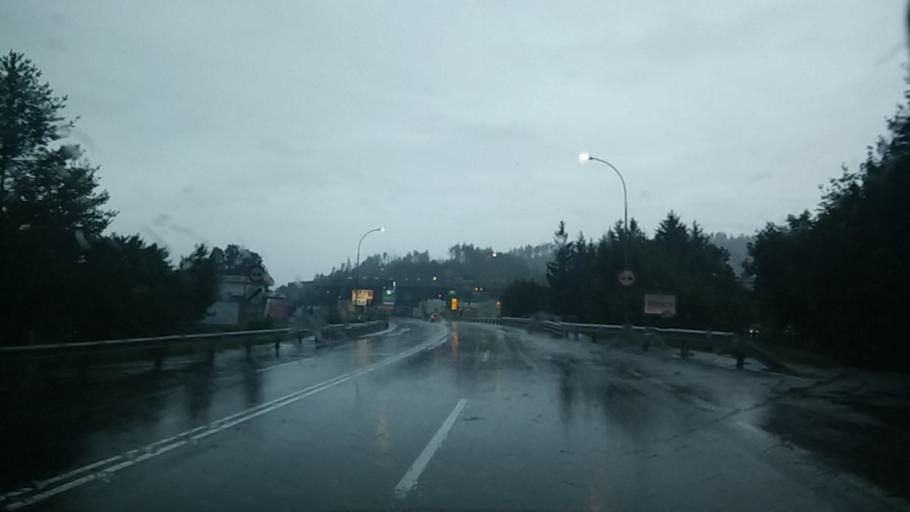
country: AT
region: Carinthia
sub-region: Villach Stadt
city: Villach
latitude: 46.6273
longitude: 13.8826
